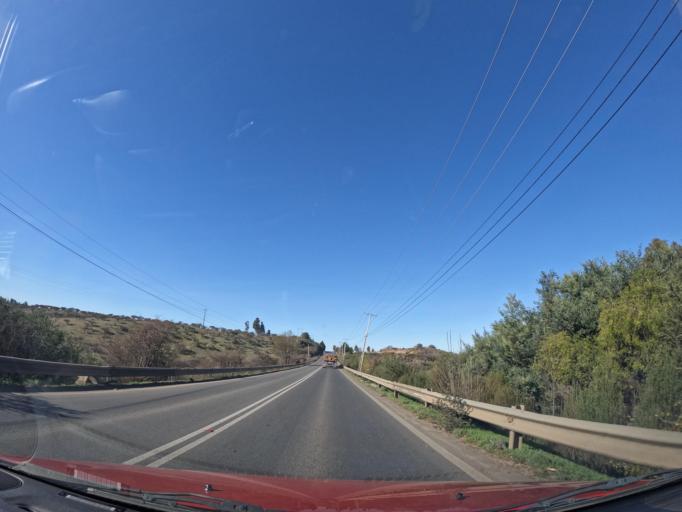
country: CL
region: Maule
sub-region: Provincia de Cauquenes
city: Cauquenes
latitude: -35.9604
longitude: -72.2588
